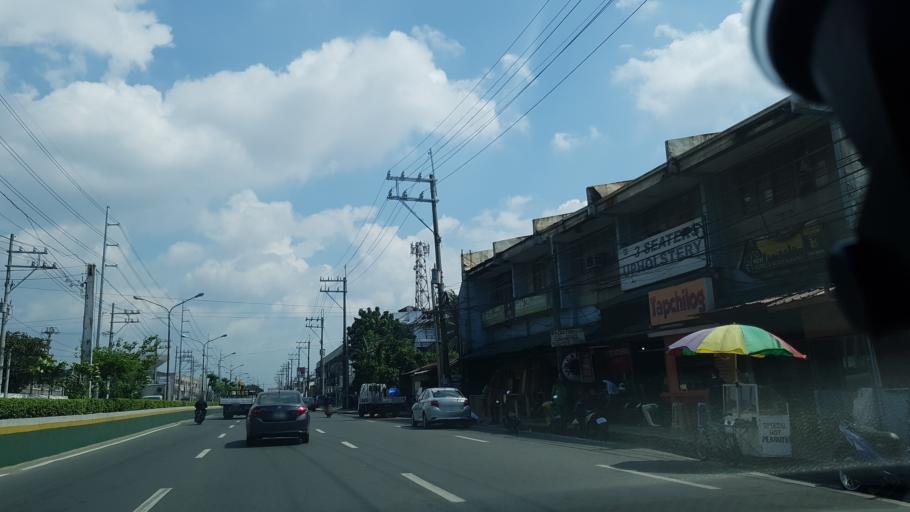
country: PH
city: Sambayanihan People's Village
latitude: 14.4844
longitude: 120.9943
